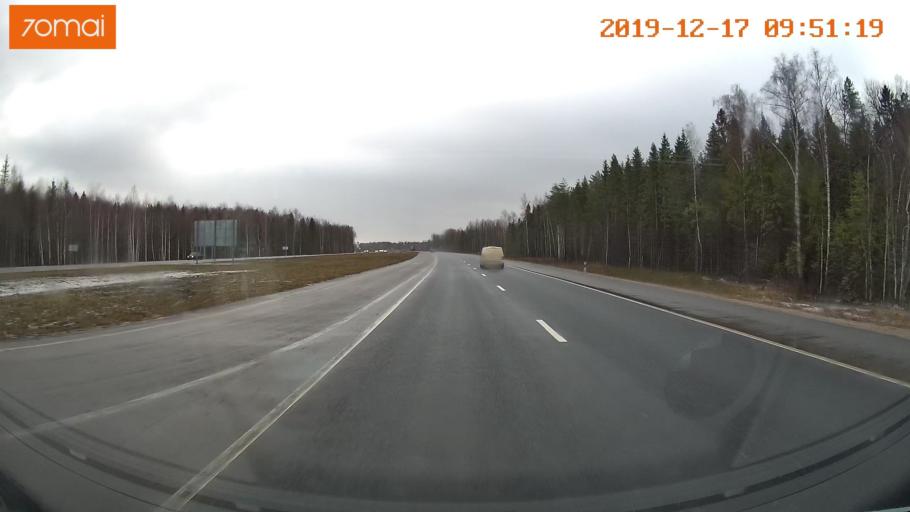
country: RU
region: Vladimir
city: Kommunar
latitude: 56.0461
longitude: 40.5190
